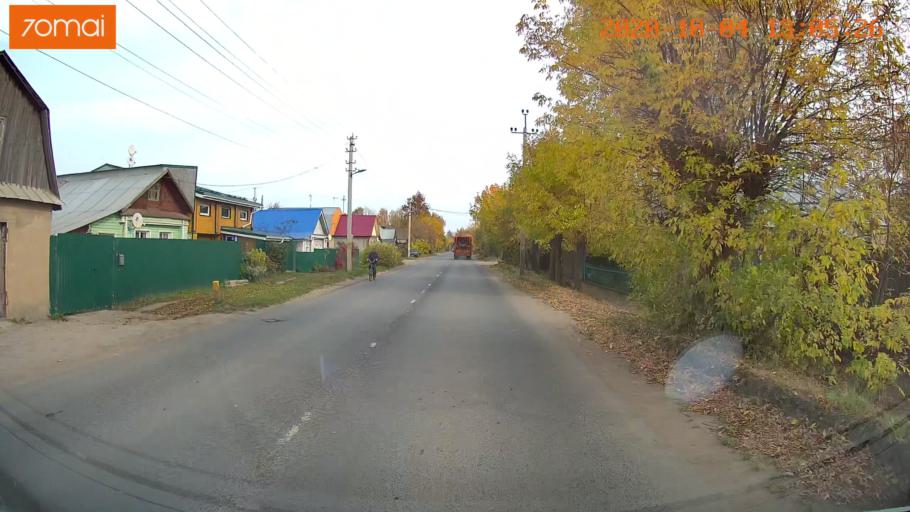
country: RU
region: Ivanovo
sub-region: Gorod Ivanovo
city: Ivanovo
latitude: 57.0422
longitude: 40.9552
